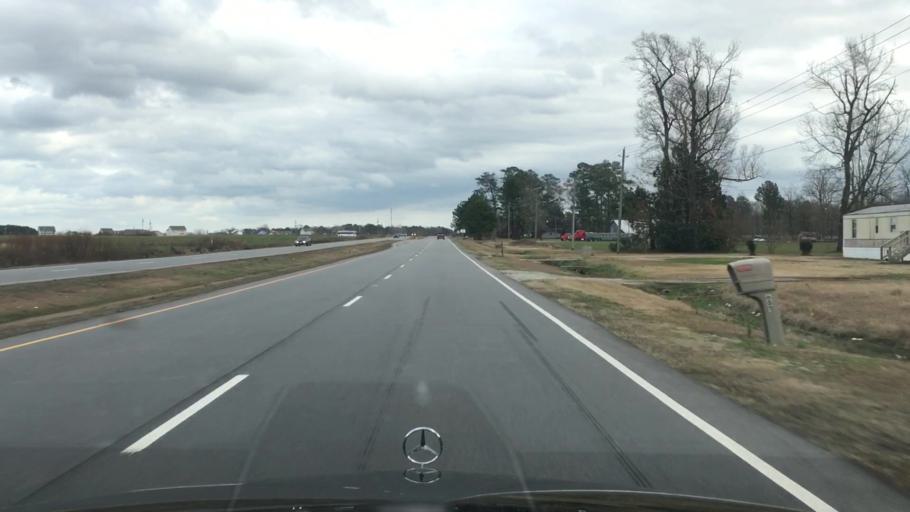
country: US
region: North Carolina
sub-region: Onslow County
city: Richlands
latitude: 34.9180
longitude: -77.6129
